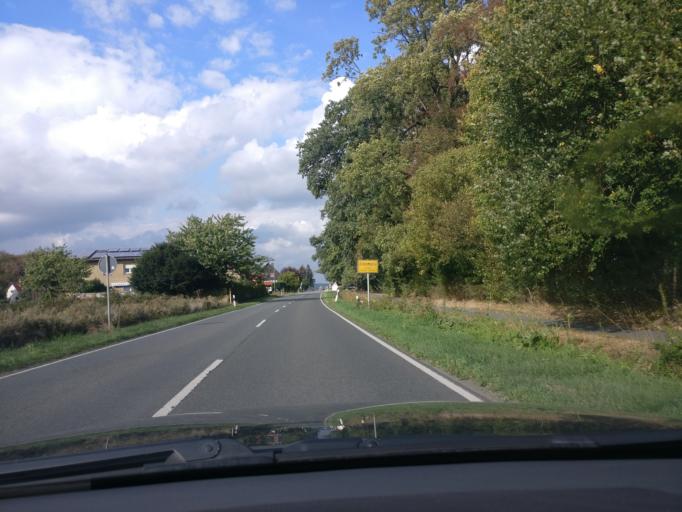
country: DE
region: Lower Saxony
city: Melle
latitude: 52.1764
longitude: 8.3377
